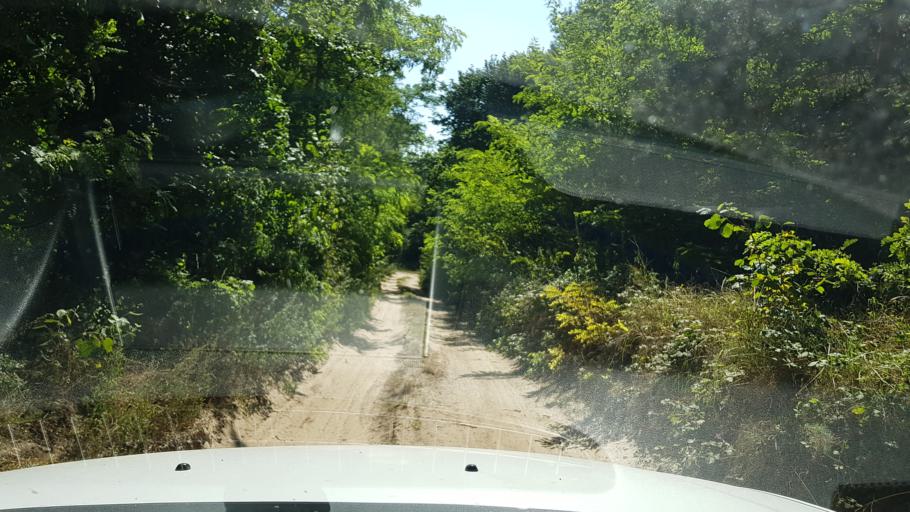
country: PL
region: West Pomeranian Voivodeship
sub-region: Powiat gryfinski
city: Cedynia
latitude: 52.8349
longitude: 14.2516
